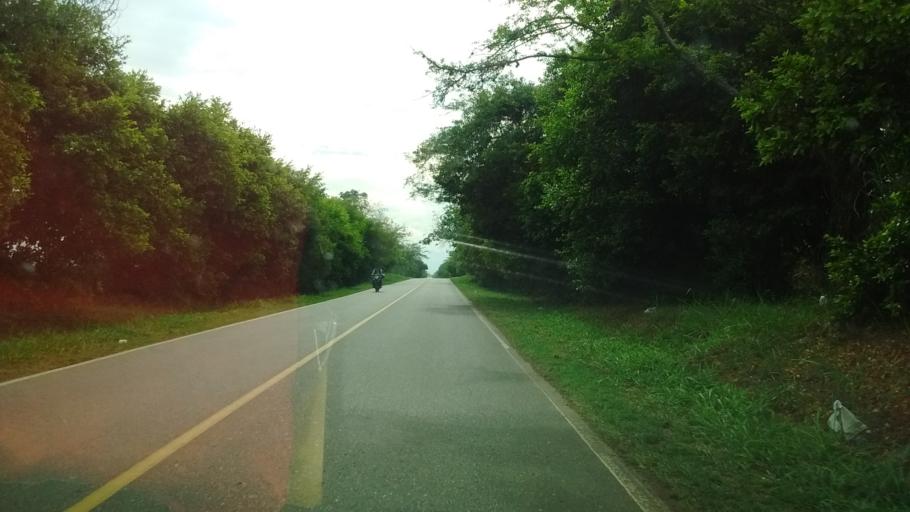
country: CO
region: Cauca
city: Caloto
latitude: 3.0467
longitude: -76.4309
